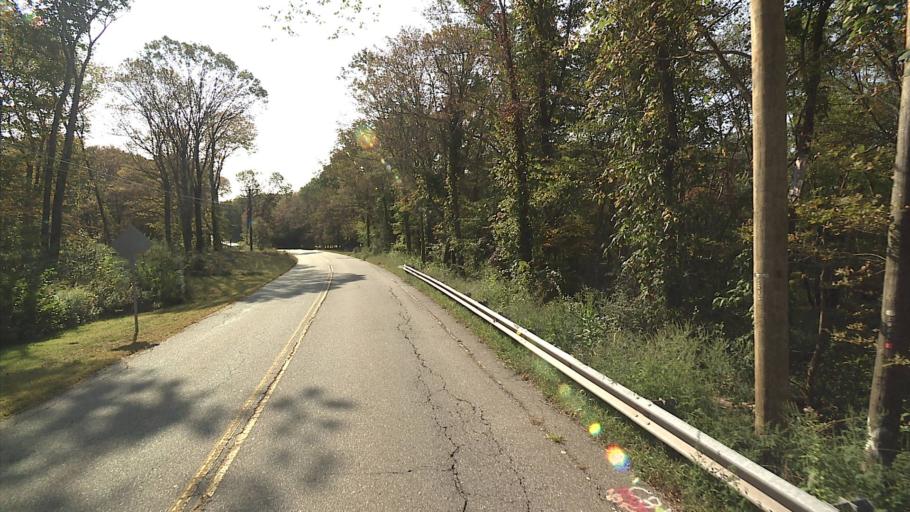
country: US
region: Connecticut
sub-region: Windham County
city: Willimantic
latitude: 41.6528
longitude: -72.2453
